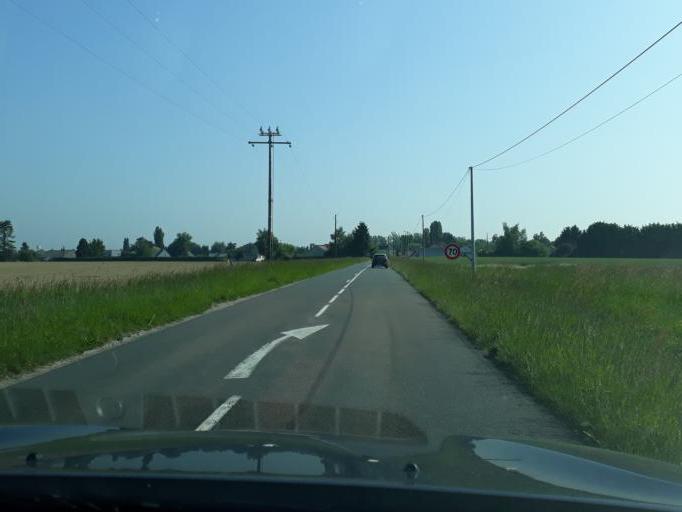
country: FR
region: Centre
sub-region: Departement du Loiret
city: Trainou
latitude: 47.9612
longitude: 2.0933
